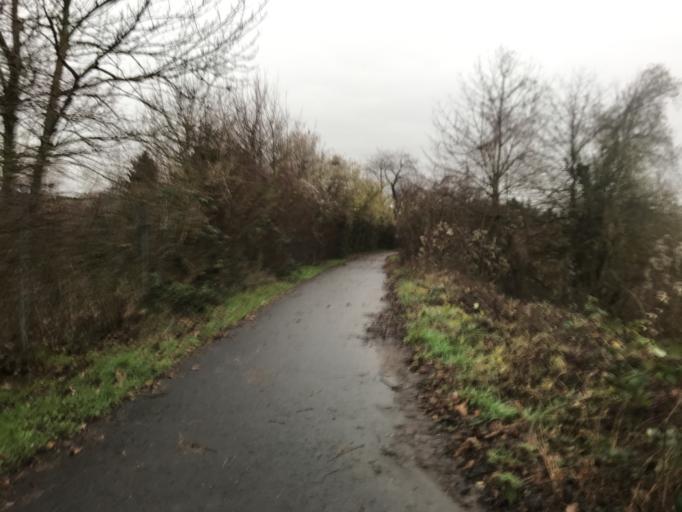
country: DE
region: Rheinland-Pfalz
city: Mommenheim
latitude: 49.8820
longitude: 8.2744
